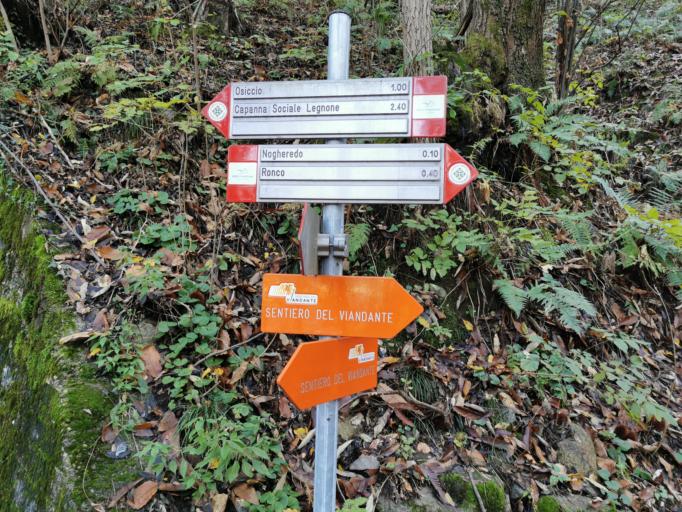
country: IT
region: Lombardy
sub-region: Provincia di Sondrio
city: Delebio
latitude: 46.1284
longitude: 9.4590
